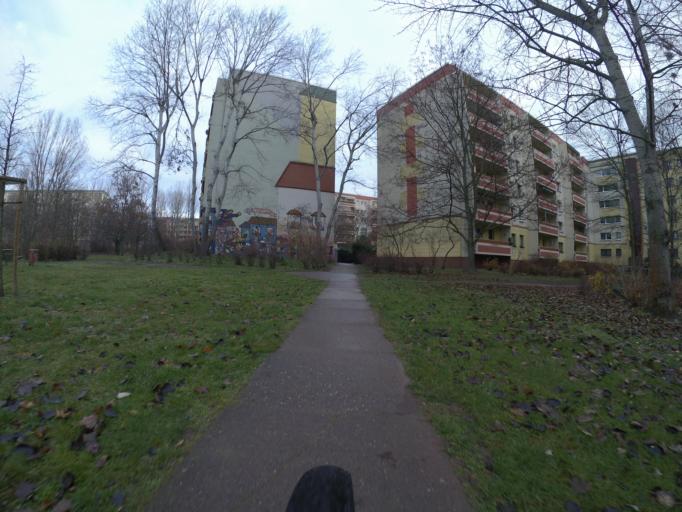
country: DE
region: Berlin
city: Marzahn
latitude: 52.5534
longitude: 13.5705
